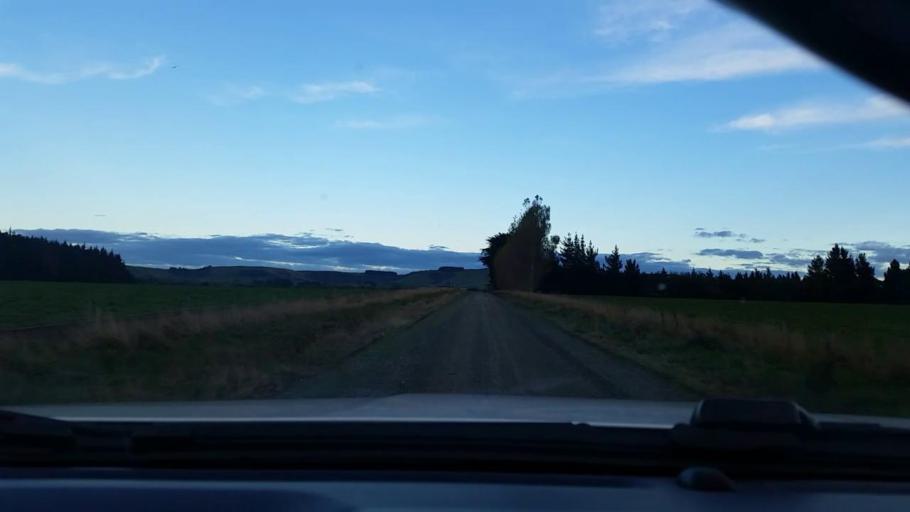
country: NZ
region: Southland
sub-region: Southland District
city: Winton
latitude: -46.1051
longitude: 168.4554
